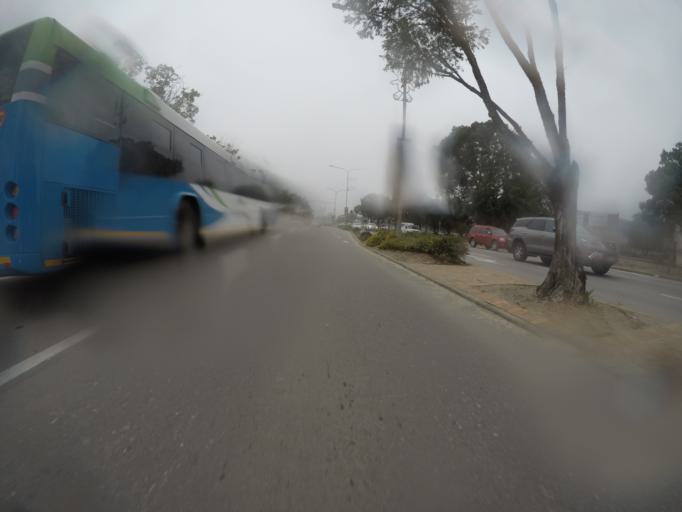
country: ZA
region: Western Cape
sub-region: Eden District Municipality
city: George
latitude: -33.9727
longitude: 22.4458
